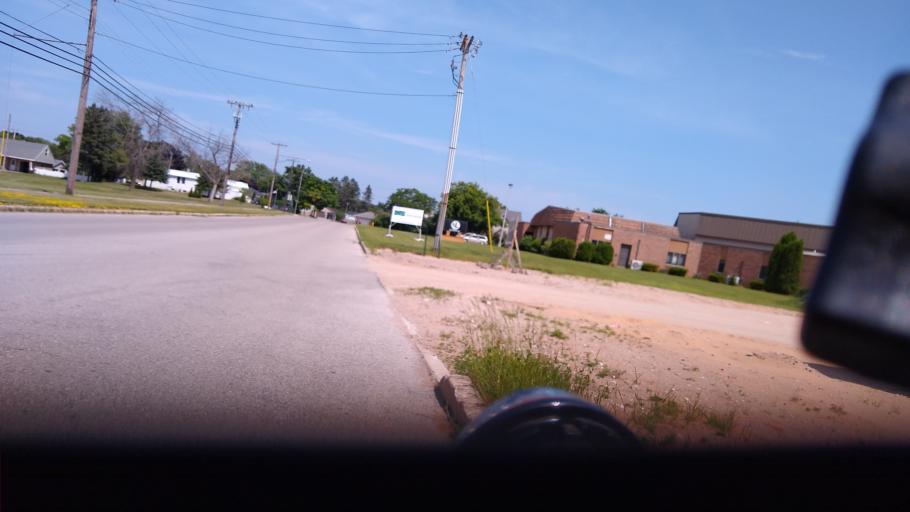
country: US
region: Michigan
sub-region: Delta County
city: Escanaba
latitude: 45.7355
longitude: -87.0769
